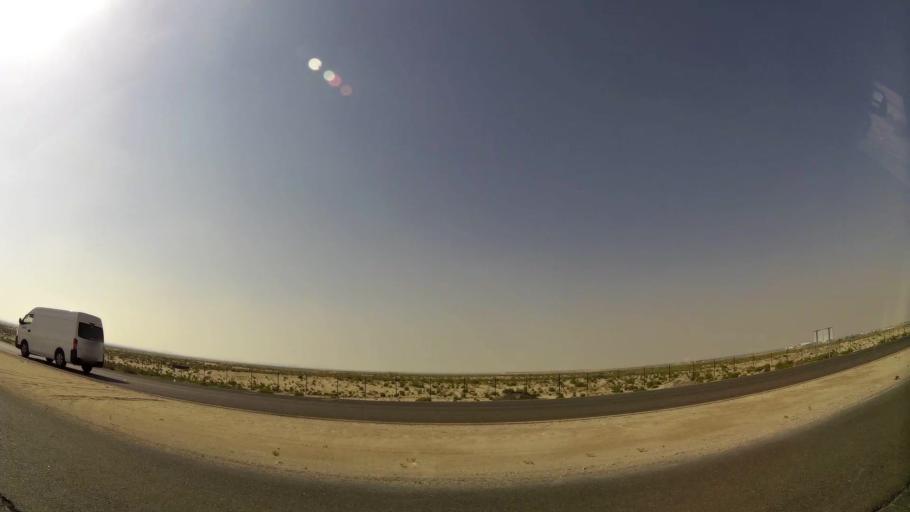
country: AE
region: Dubai
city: Dubai
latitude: 24.9585
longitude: 55.0176
